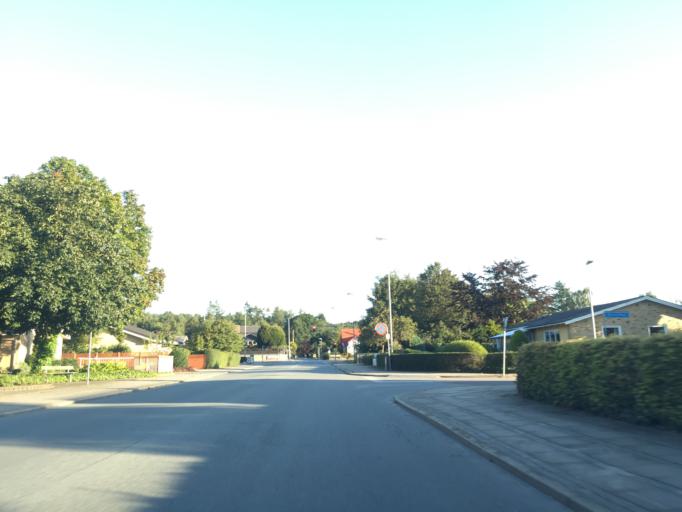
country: DK
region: Central Jutland
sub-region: Viborg Kommune
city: Bjerringbro
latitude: 56.3782
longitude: 9.6535
